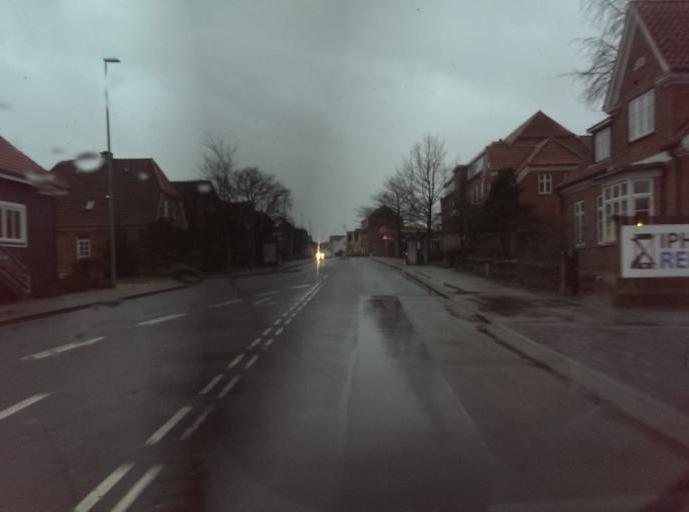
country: DK
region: South Denmark
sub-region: Esbjerg Kommune
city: Esbjerg
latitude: 55.4791
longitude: 8.4611
